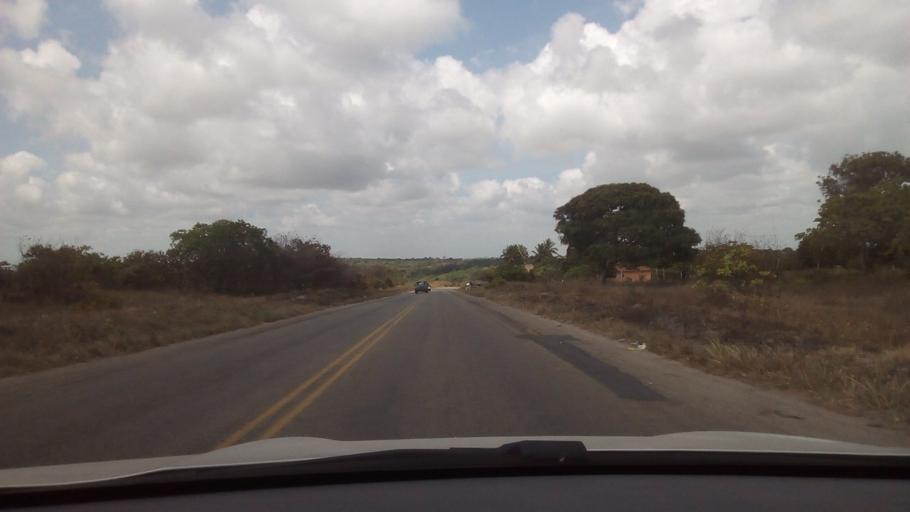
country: BR
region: Paraiba
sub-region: Conde
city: Conde
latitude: -7.2530
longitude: -34.8141
